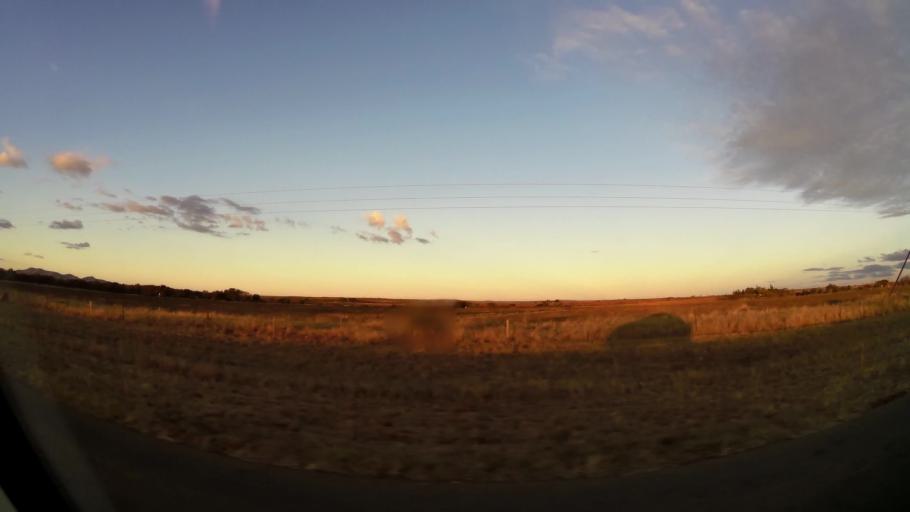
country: ZA
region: Limpopo
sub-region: Capricorn District Municipality
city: Polokwane
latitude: -23.7743
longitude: 29.4736
